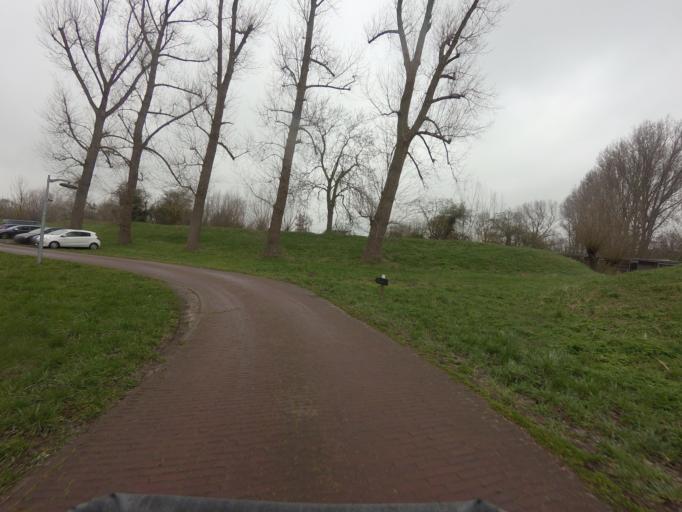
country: NL
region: Utrecht
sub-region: Stichtse Vecht
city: Breukelen
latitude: 52.1967
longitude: 5.0056
